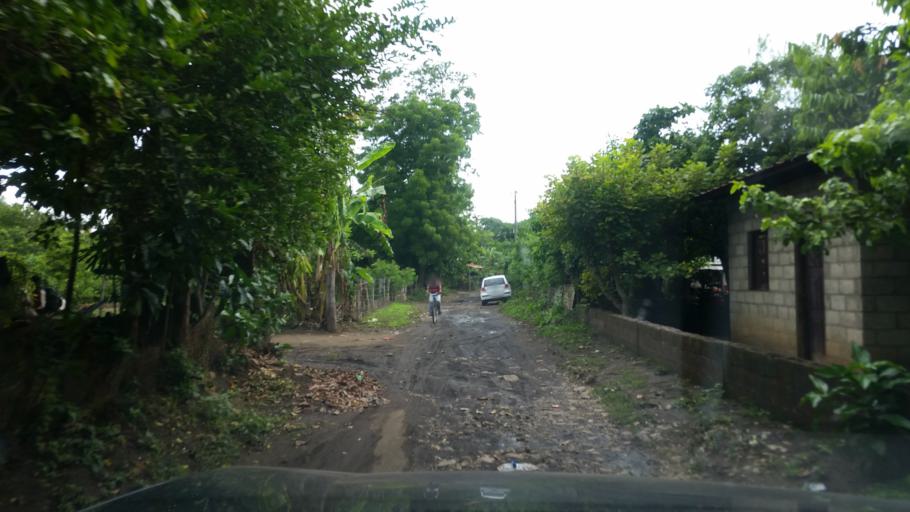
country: NI
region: Chinandega
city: Puerto Morazan
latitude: 12.7672
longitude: -87.1273
